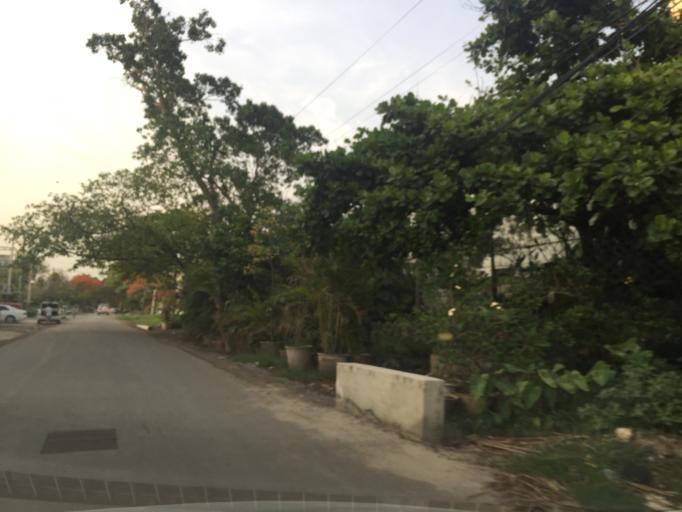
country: MM
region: Mandalay
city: Mandalay
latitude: 21.9714
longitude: 96.1014
